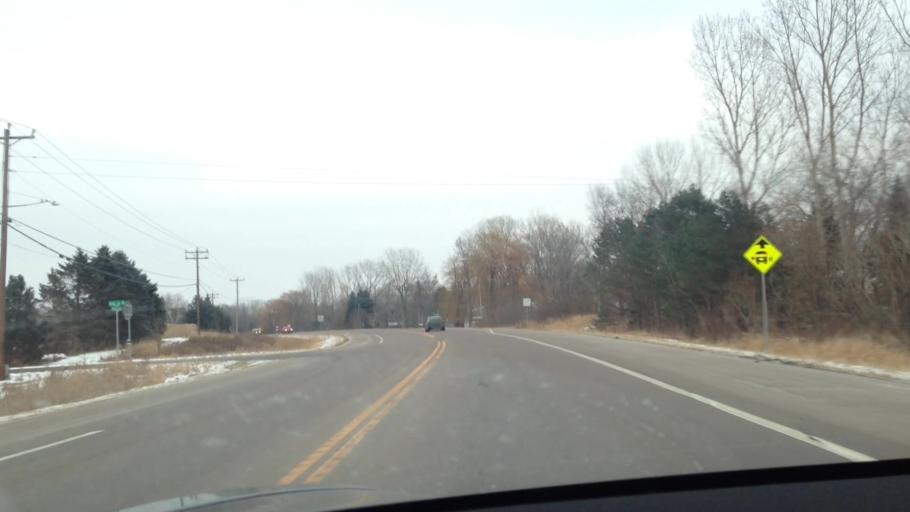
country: US
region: Minnesota
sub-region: Washington County
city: Forest Lake
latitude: 45.2609
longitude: -92.9534
